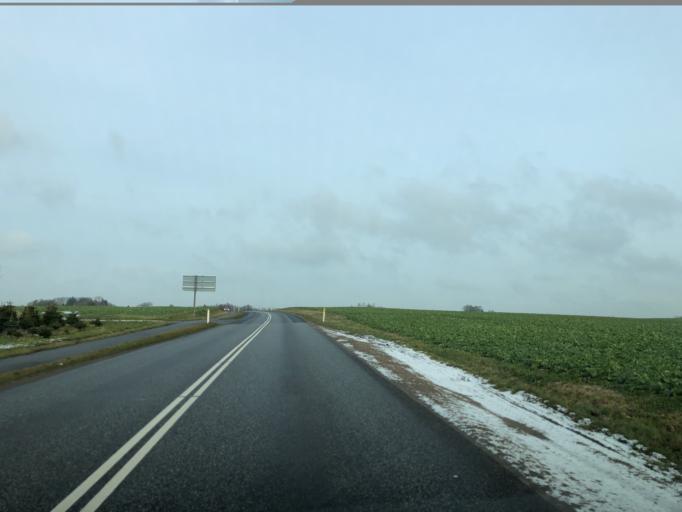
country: DK
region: South Denmark
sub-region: Vejle Kommune
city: Jelling
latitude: 55.7687
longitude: 9.4243
